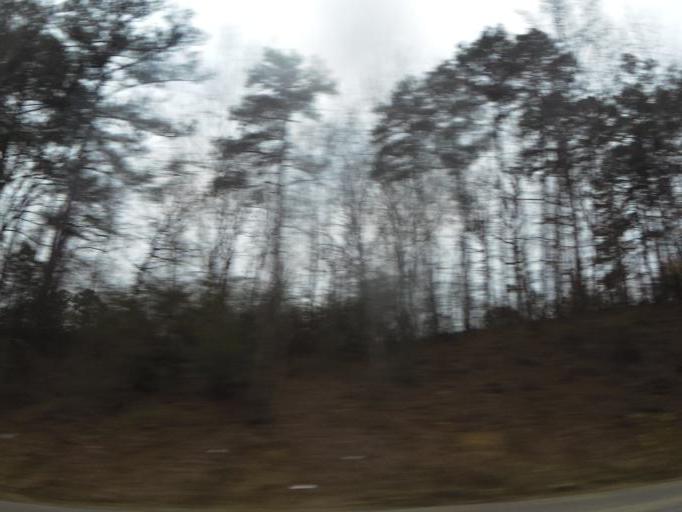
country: US
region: Alabama
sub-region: Blount County
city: Smoke Rise
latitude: 33.8543
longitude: -86.8296
